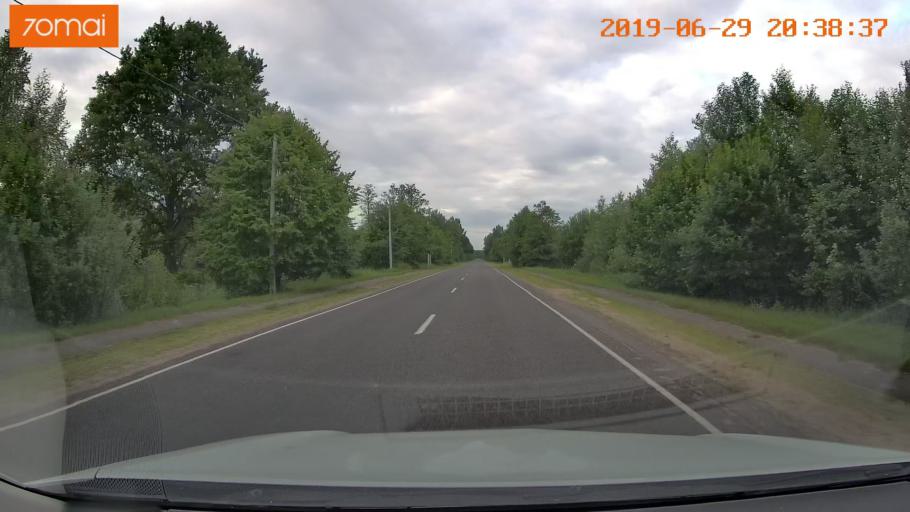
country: BY
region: Brest
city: Hantsavichy
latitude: 52.5520
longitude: 26.3643
